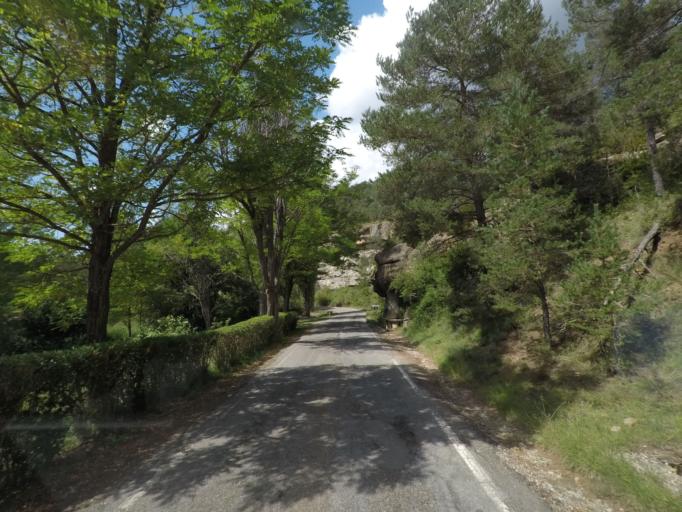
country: ES
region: Aragon
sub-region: Provincia de Huesca
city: Yebra de Basa
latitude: 42.4085
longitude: -0.1991
